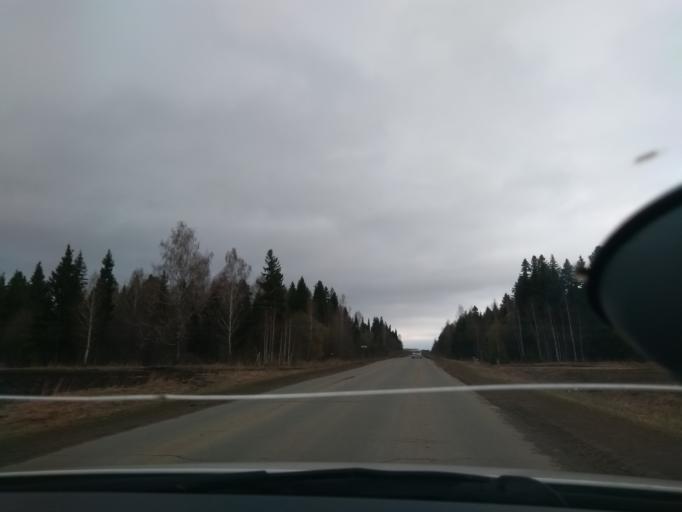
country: RU
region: Perm
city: Kungur
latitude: 57.3956
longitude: 56.8752
